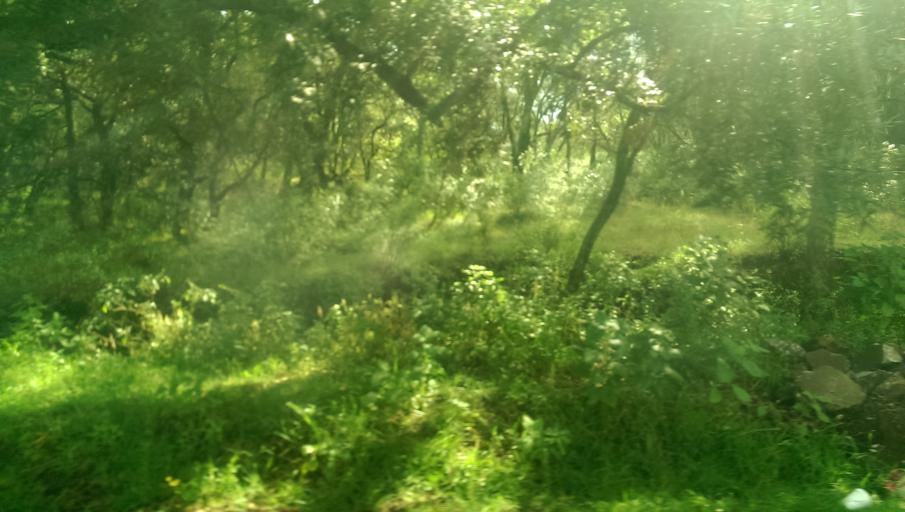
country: MX
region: Mexico
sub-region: Jilotepec
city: Jilotepec de Molina Enriquez
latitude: 19.9253
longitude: -99.4948
